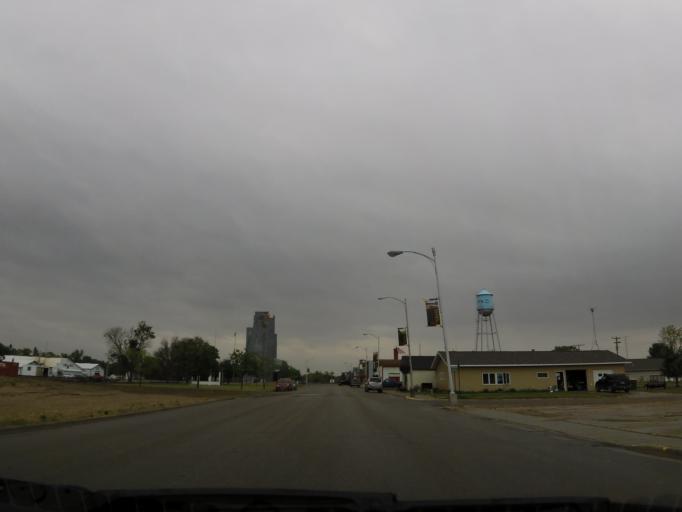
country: US
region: Minnesota
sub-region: Marshall County
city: Warren
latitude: 48.4516
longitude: -96.8747
